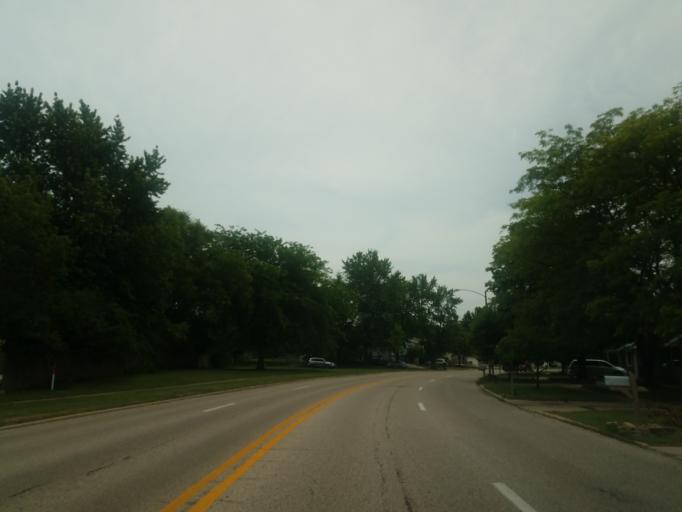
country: US
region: Illinois
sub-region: McLean County
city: Normal
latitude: 40.4993
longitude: -88.9387
